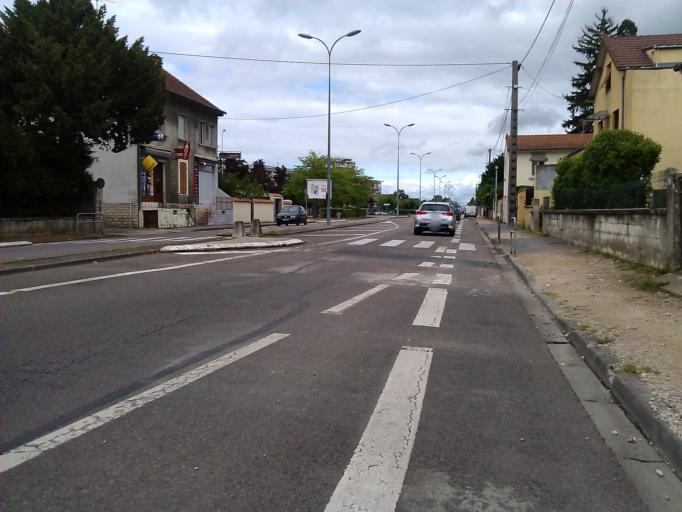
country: FR
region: Bourgogne
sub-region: Departement de Saone-et-Loire
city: Champforgeuil
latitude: 46.8032
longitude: 4.8455
